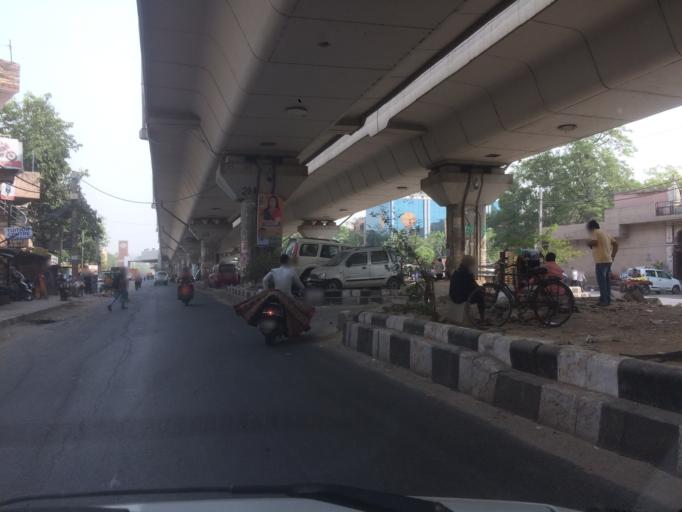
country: IN
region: NCT
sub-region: Central Delhi
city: Karol Bagh
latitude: 28.6236
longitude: 77.1351
